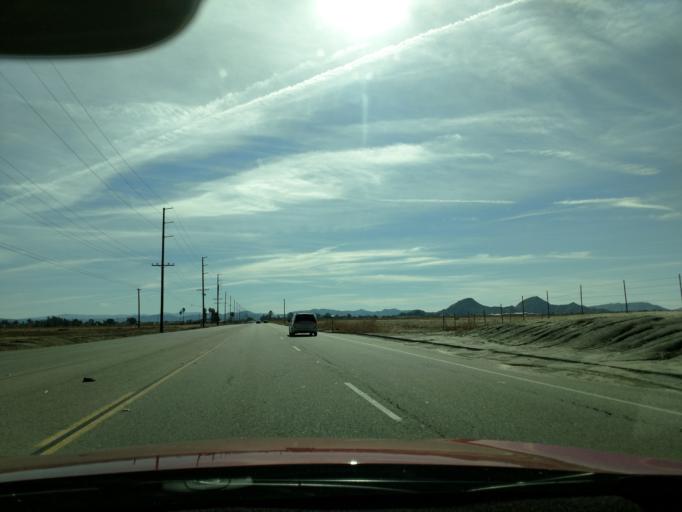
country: US
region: California
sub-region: Riverside County
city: San Jacinto
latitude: 33.7972
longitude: -117.0068
